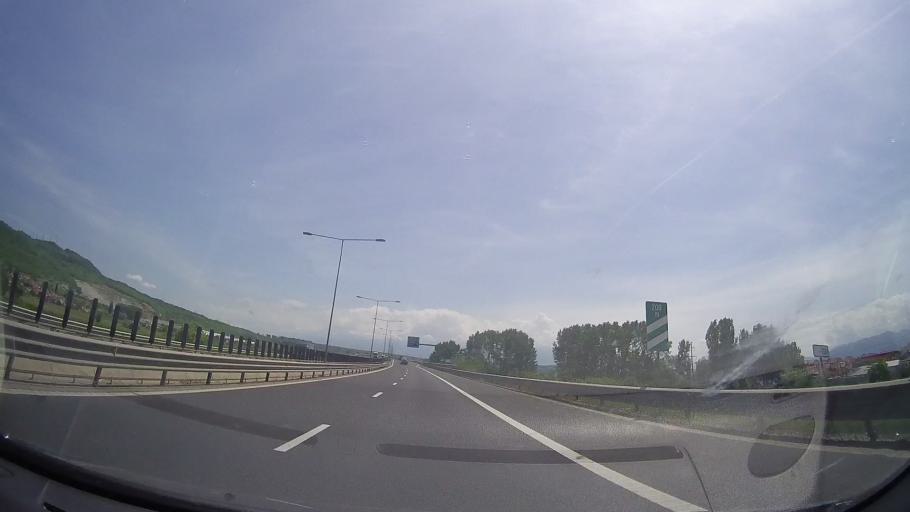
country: RO
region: Sibiu
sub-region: Municipiul Sibiu
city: Sibiu
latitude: 45.8045
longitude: 24.1801
